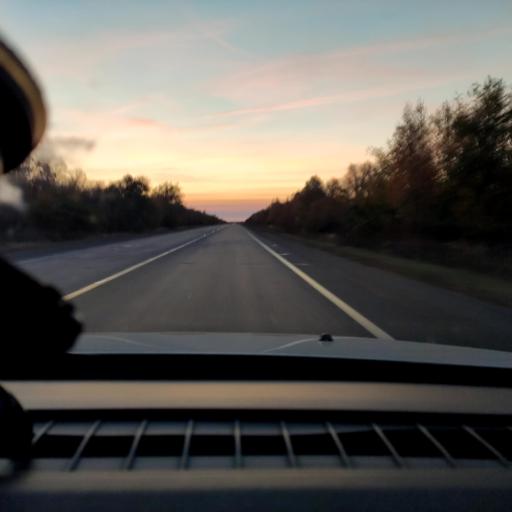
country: RU
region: Samara
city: Chapayevsk
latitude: 52.9893
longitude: 49.8505
